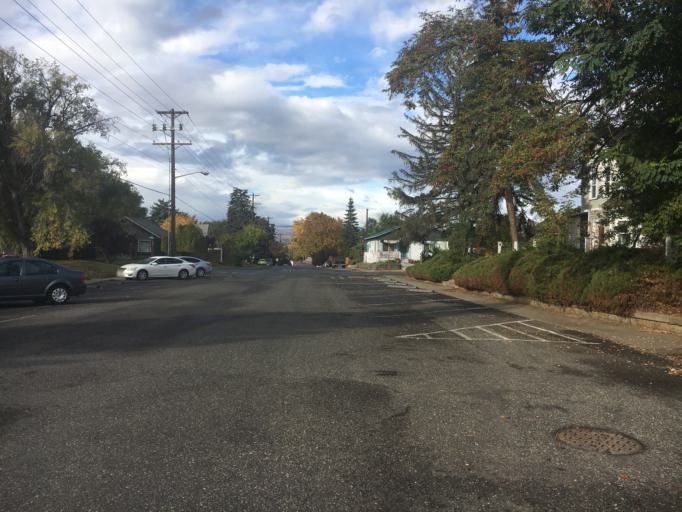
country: US
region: Washington
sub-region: Kittitas County
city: Ellensburg
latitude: 46.9975
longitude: -120.5507
